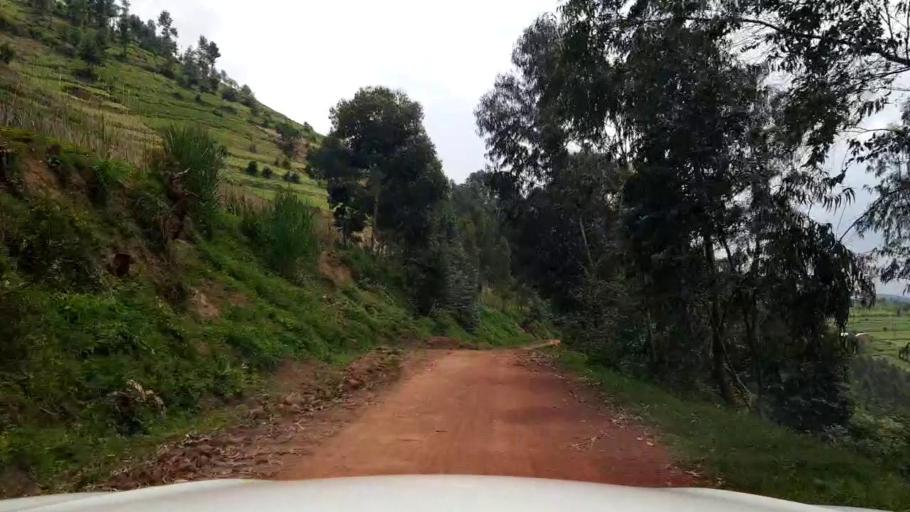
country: RW
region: Northern Province
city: Byumba
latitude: -1.4820
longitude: 29.9219
